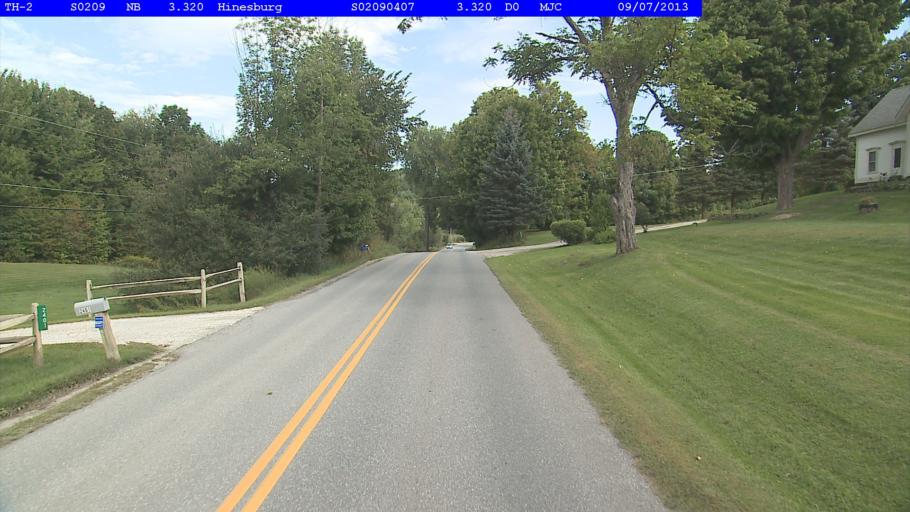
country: US
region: Vermont
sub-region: Chittenden County
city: Hinesburg
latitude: 44.3589
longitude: -73.0743
